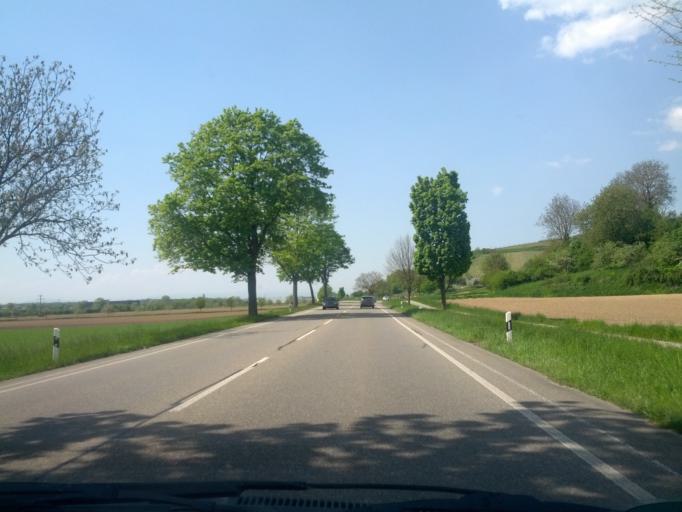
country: DE
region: Baden-Wuerttemberg
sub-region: Freiburg Region
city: Malterdingen
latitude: 48.1447
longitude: 7.7934
